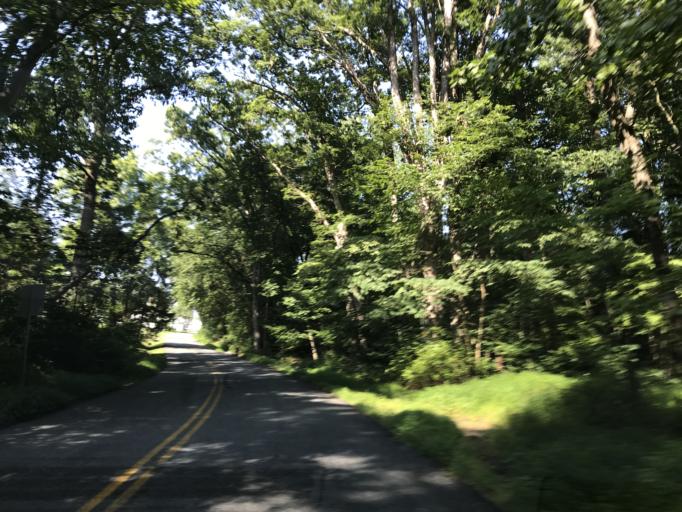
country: US
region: Maryland
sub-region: Harford County
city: South Bel Air
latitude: 39.6188
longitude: -76.2809
